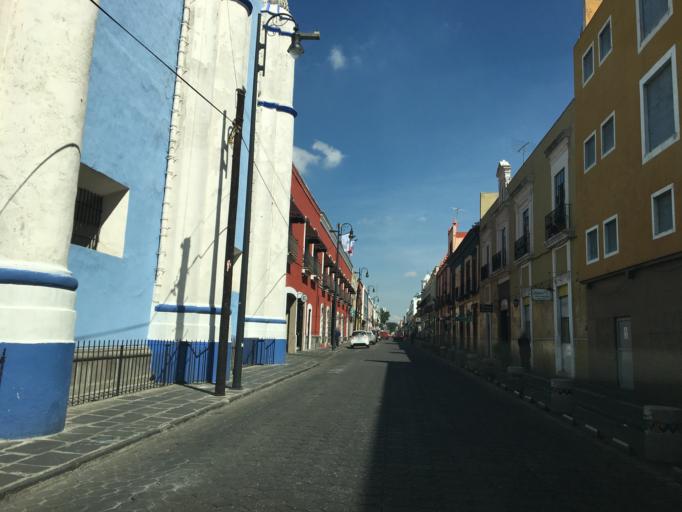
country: MX
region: Puebla
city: Puebla
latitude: 19.0424
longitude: -98.2004
